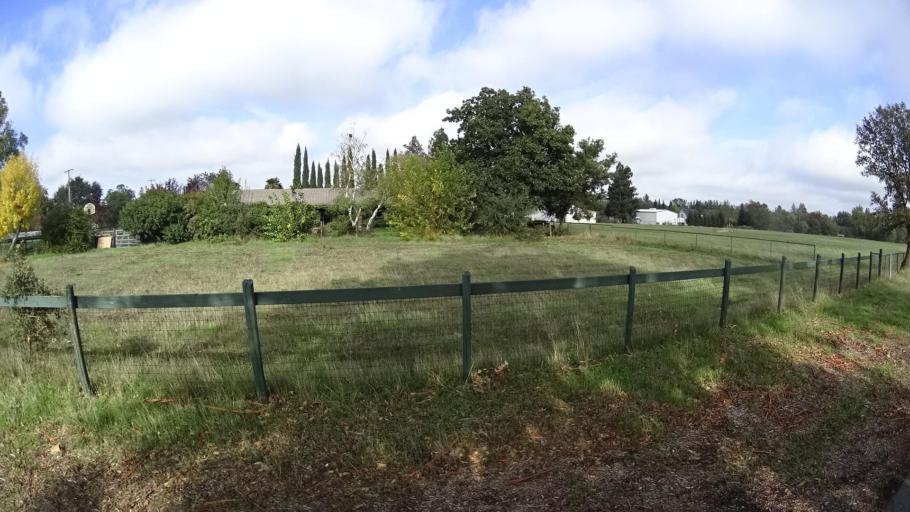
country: US
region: California
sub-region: Sacramento County
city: Vineyard
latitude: 38.4344
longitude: -121.3157
